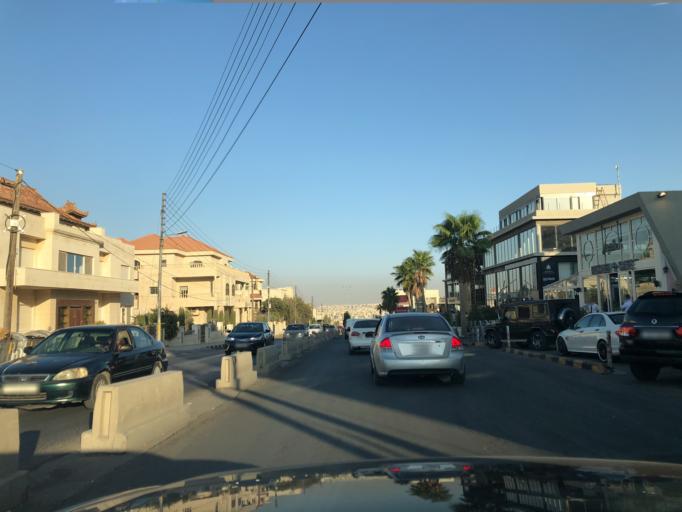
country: JO
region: Amman
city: Al Bunayyat ash Shamaliyah
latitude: 31.9422
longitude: 35.8809
